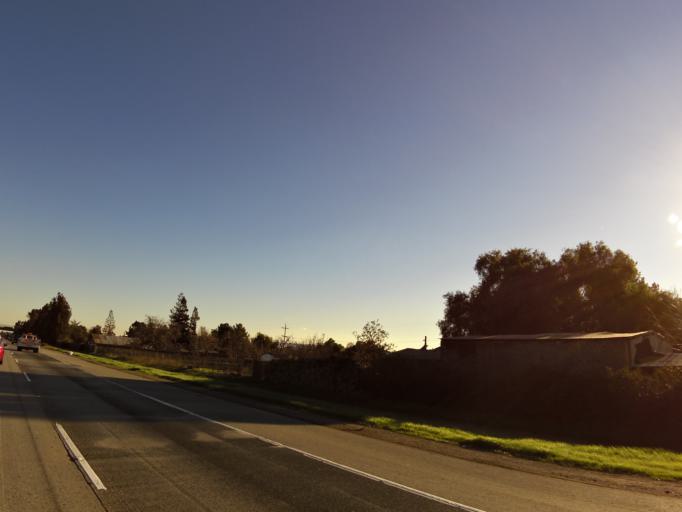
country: US
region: California
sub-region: Santa Clara County
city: Morgan Hill
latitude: 37.1441
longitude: -121.6441
